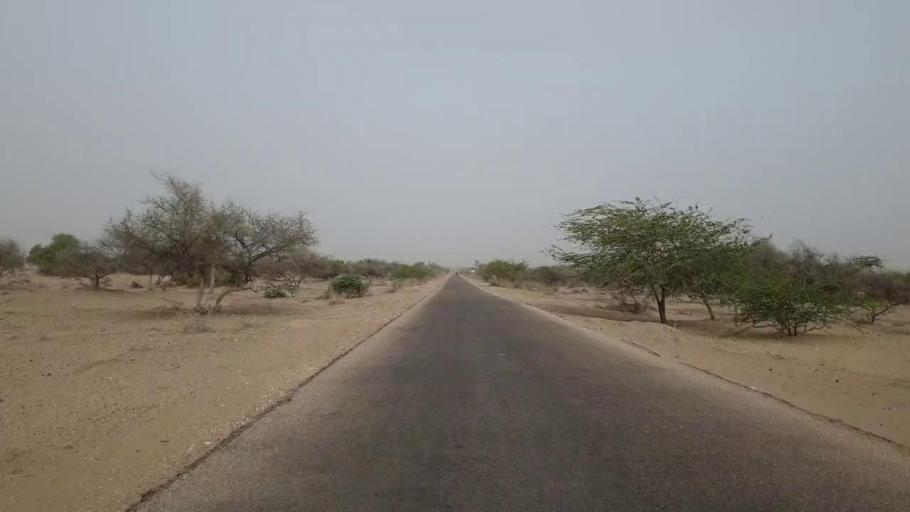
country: PK
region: Sindh
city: Islamkot
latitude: 24.5766
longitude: 70.3108
